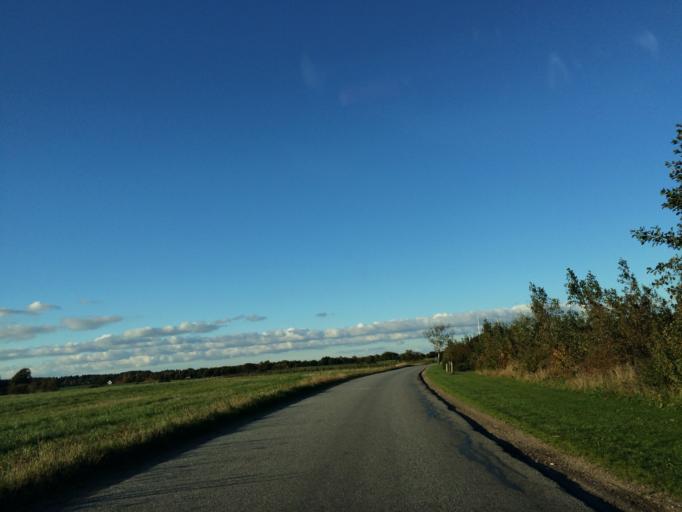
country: DK
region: Central Jutland
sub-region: Silkeborg Kommune
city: Svejbaek
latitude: 56.1798
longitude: 9.6921
